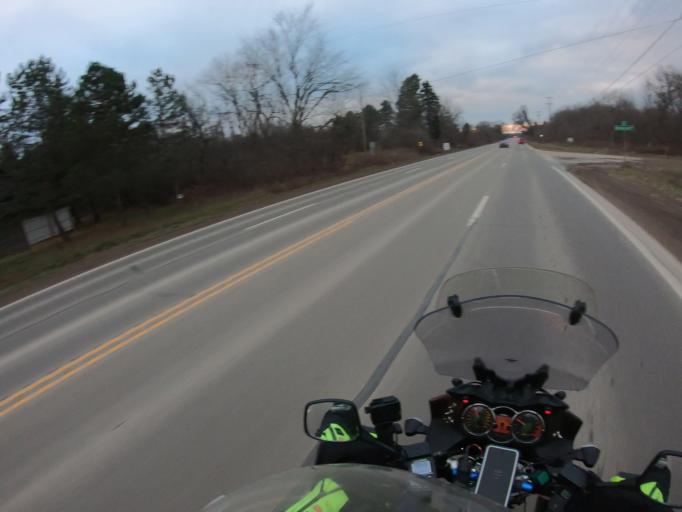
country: US
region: Michigan
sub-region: Oakland County
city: Holly
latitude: 42.8597
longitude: -83.5795
